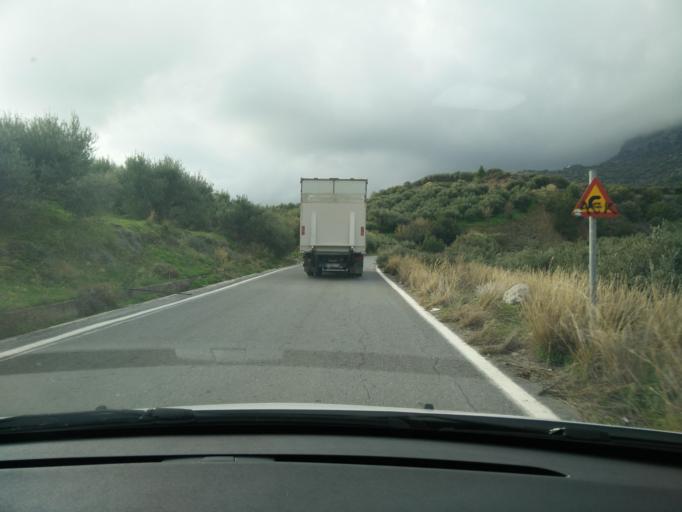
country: GR
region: Crete
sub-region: Nomos Lasithiou
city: Gra Liyia
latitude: 35.0225
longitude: 25.5712
